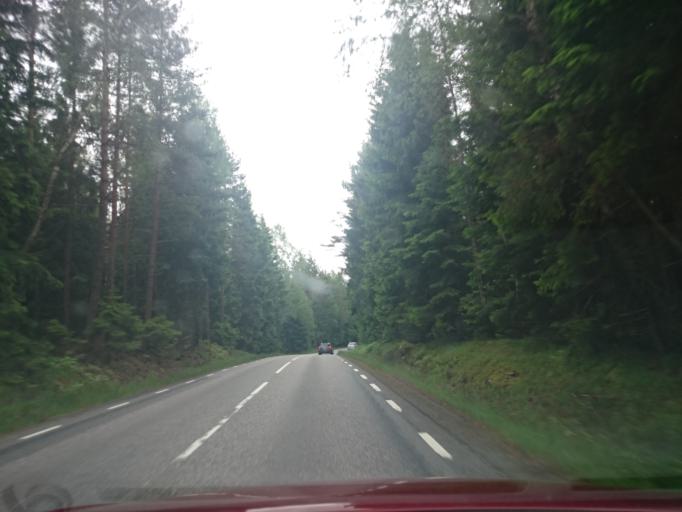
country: SE
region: Vaestra Goetaland
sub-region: Harryda Kommun
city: Hindas
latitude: 57.7050
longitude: 12.3525
